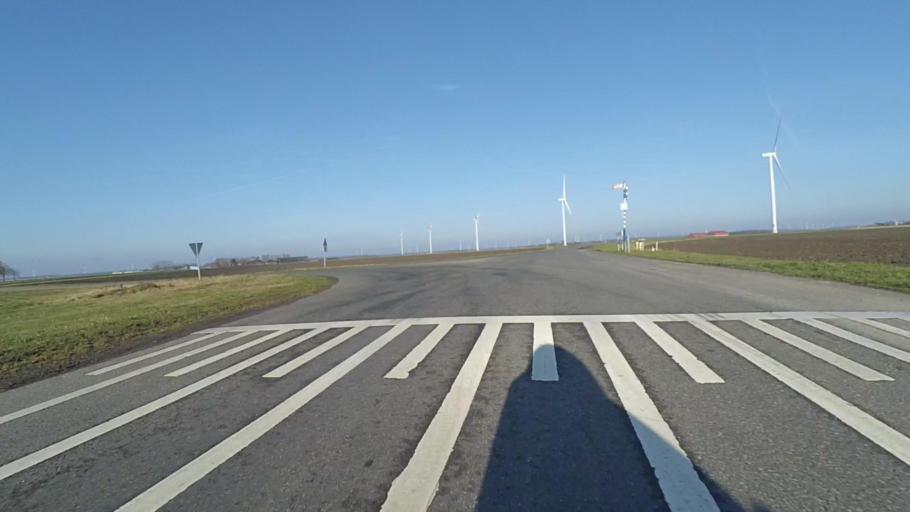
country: NL
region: Utrecht
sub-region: Gemeente Bunschoten
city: Spakenburg
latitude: 52.2962
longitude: 5.3906
